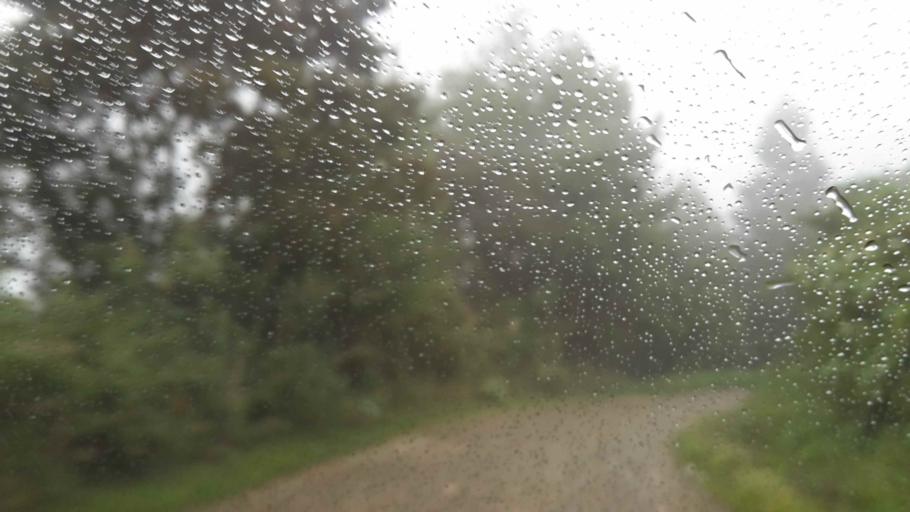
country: BO
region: Cochabamba
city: Colomi
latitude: -17.1494
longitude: -65.9116
